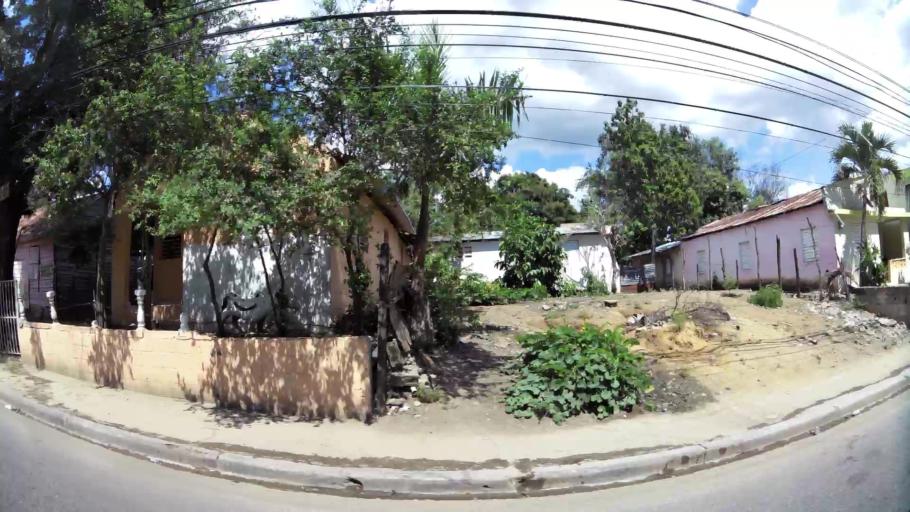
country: DO
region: Santiago
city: Santiago de los Caballeros
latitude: 19.4094
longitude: -70.6718
